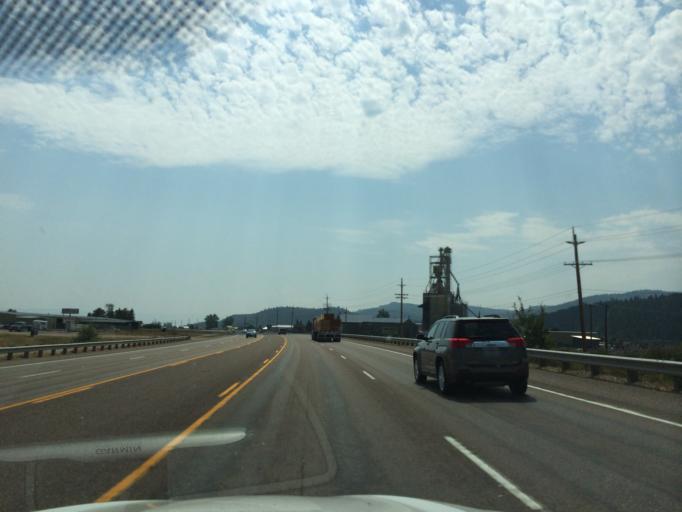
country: US
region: Montana
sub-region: Flathead County
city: Kalispell
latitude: 48.1461
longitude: -114.2861
